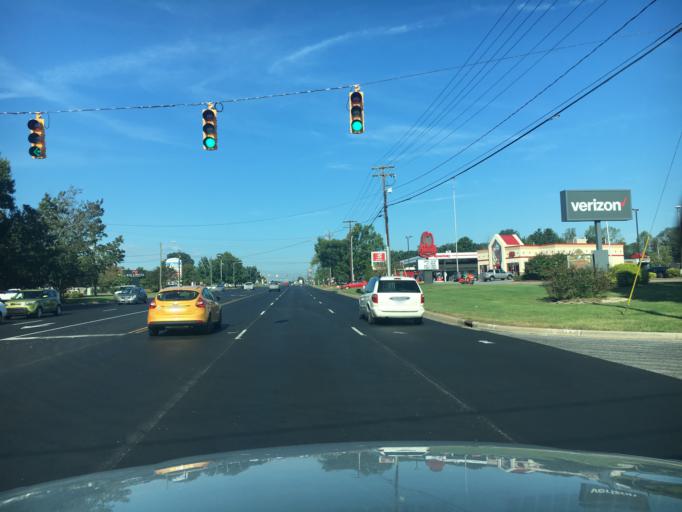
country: US
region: North Carolina
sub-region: Catawba County
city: Hickory
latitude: 35.7068
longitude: -81.3054
